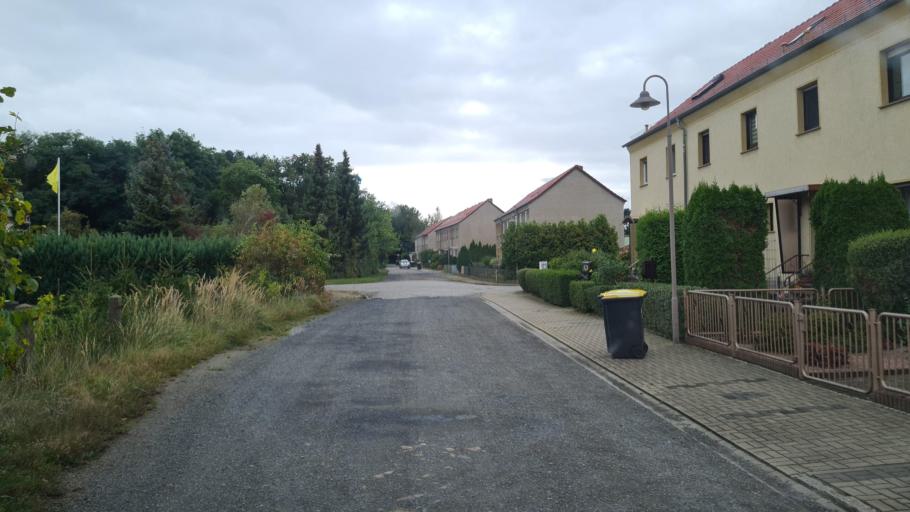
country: DE
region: Brandenburg
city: Lauchhammer
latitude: 51.5054
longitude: 13.7565
